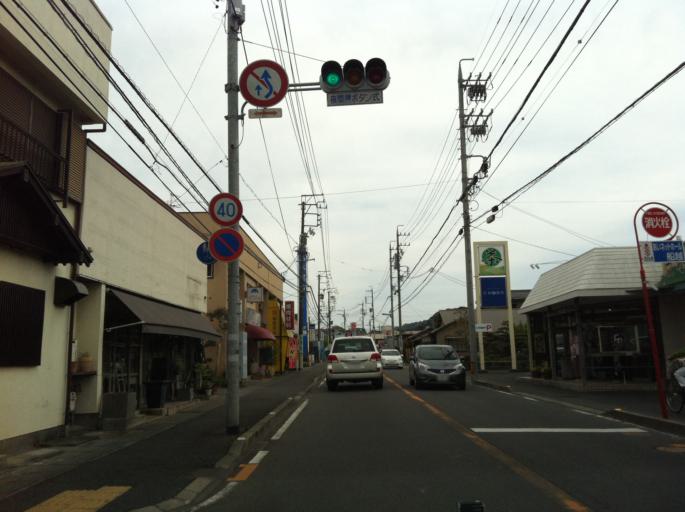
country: JP
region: Shizuoka
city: Shizuoka-shi
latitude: 35.0058
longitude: 138.4656
